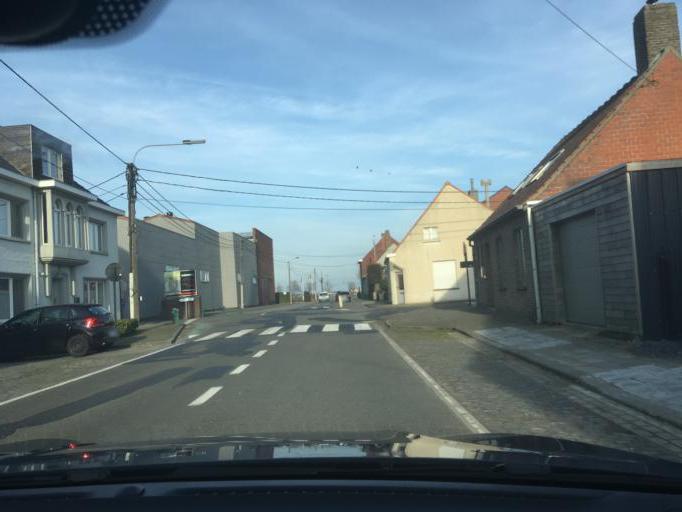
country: BE
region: Flanders
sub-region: Provincie West-Vlaanderen
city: Wielsbeke
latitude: 50.9203
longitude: 3.3733
